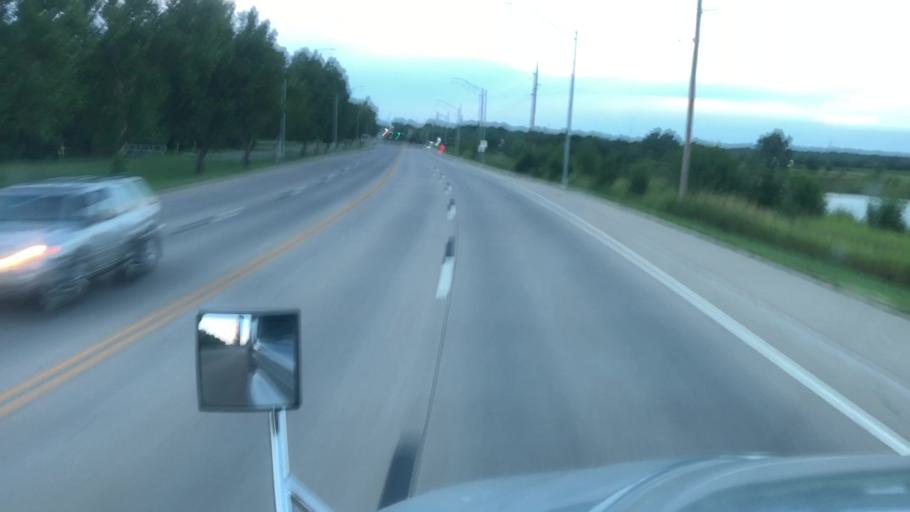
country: US
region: Oklahoma
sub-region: Kay County
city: Ponca City
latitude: 36.6903
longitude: -97.0670
